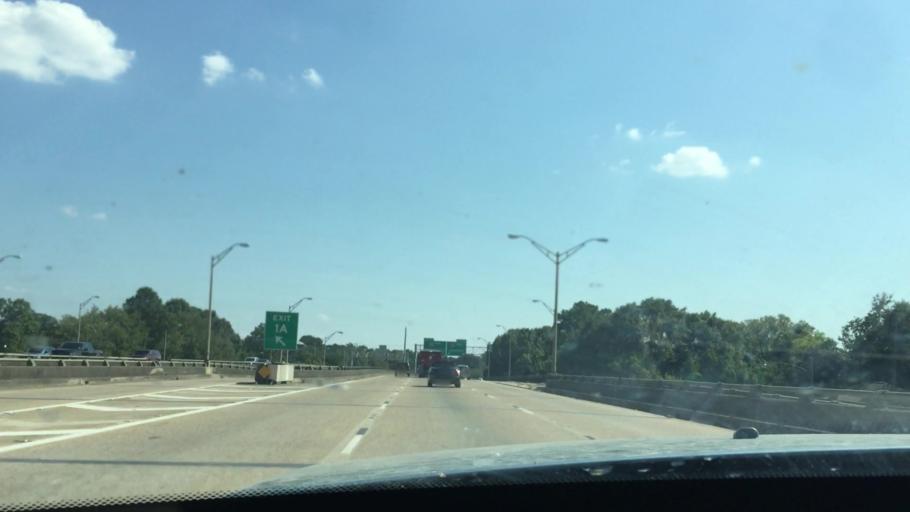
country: US
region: Louisiana
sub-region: East Baton Rouge Parish
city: Baton Rouge
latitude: 30.4464
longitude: -91.1799
